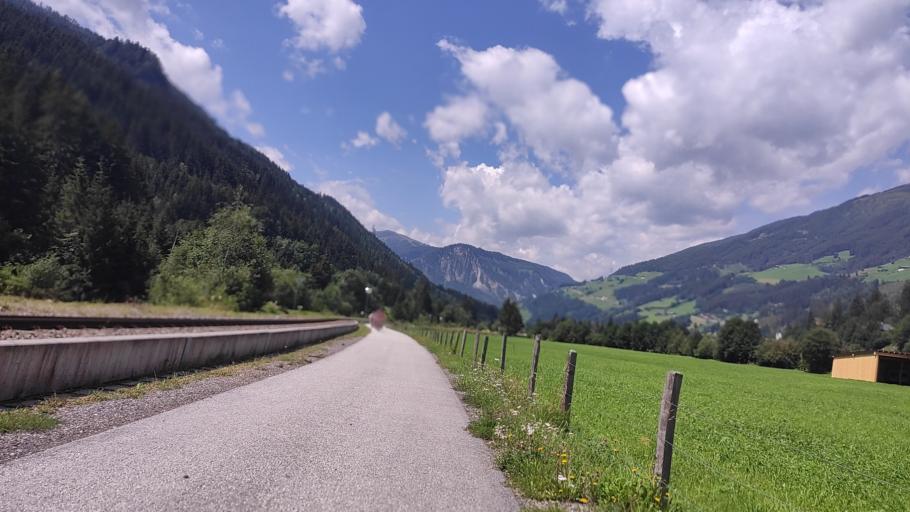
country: AT
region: Salzburg
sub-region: Politischer Bezirk Zell am See
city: Wald im Pinzgau
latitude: 47.2439
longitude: 12.2415
